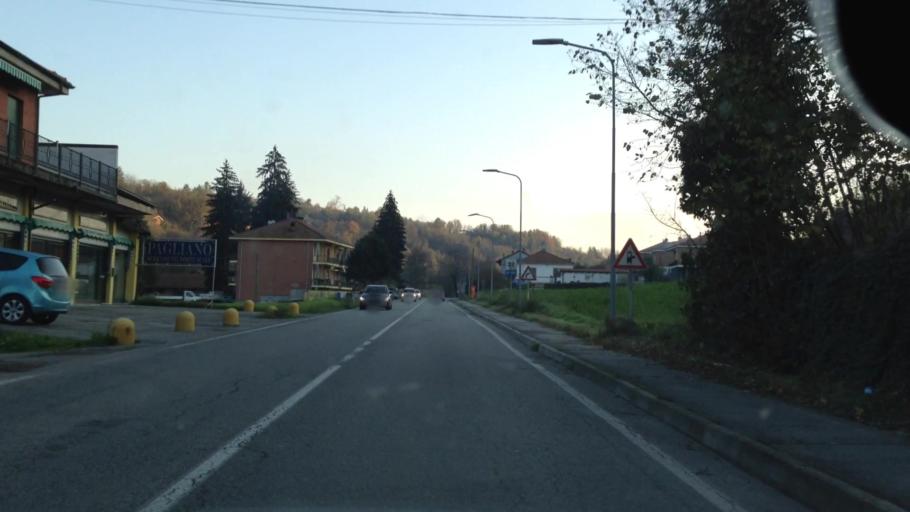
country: IT
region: Piedmont
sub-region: Provincia di Torino
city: Cavagnolo
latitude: 45.1480
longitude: 8.0542
